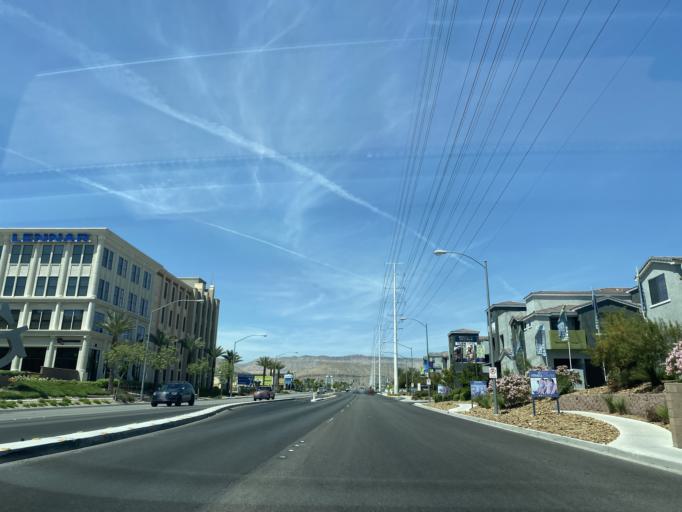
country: US
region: Nevada
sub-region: Clark County
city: Summerlin South
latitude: 36.0852
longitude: -115.2931
